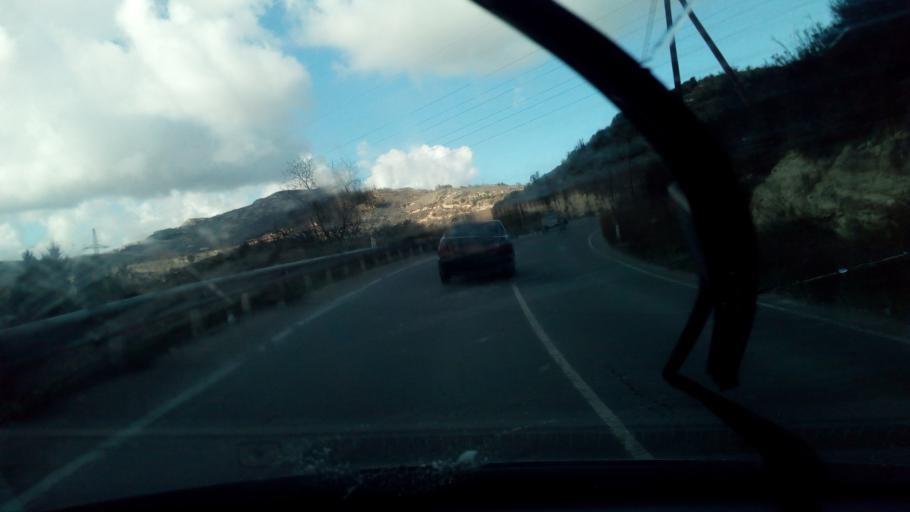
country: CY
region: Pafos
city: Tala
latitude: 34.8698
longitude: 32.4806
